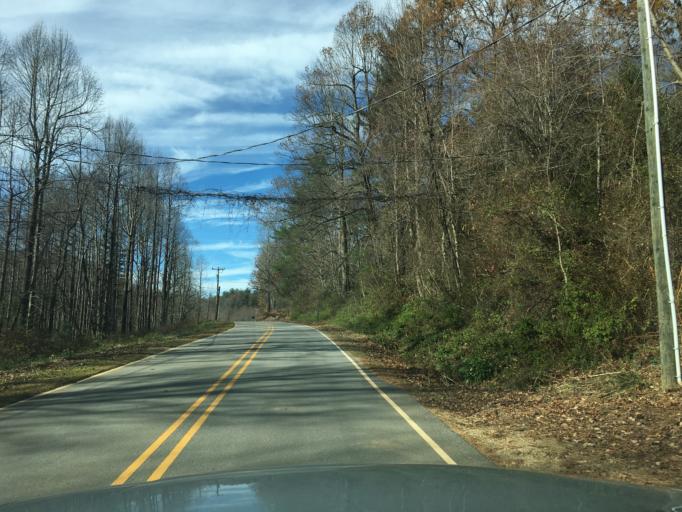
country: US
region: North Carolina
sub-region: Henderson County
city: Valley Hill
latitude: 35.2299
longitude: -82.5059
